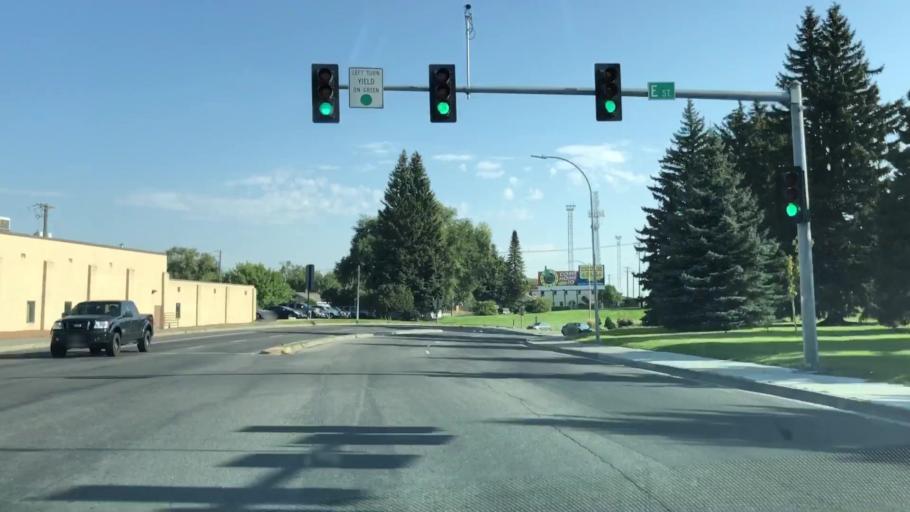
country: US
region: Idaho
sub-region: Bonneville County
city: Idaho Falls
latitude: 43.4951
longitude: -112.0360
